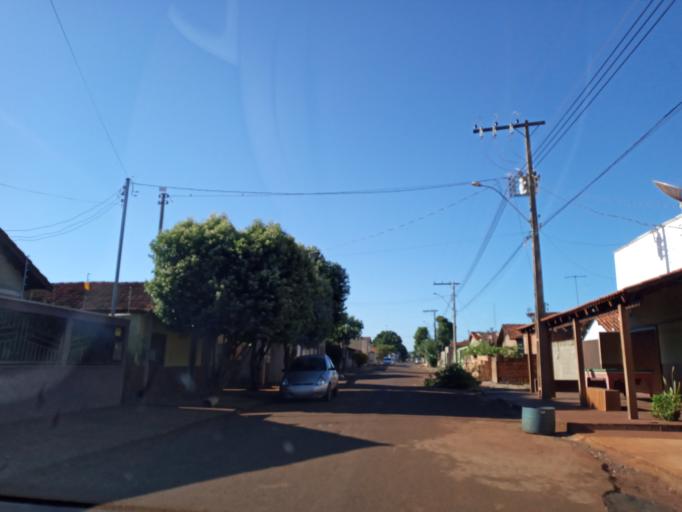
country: BR
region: Minas Gerais
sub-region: Centralina
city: Centralina
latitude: -18.5803
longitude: -49.2048
